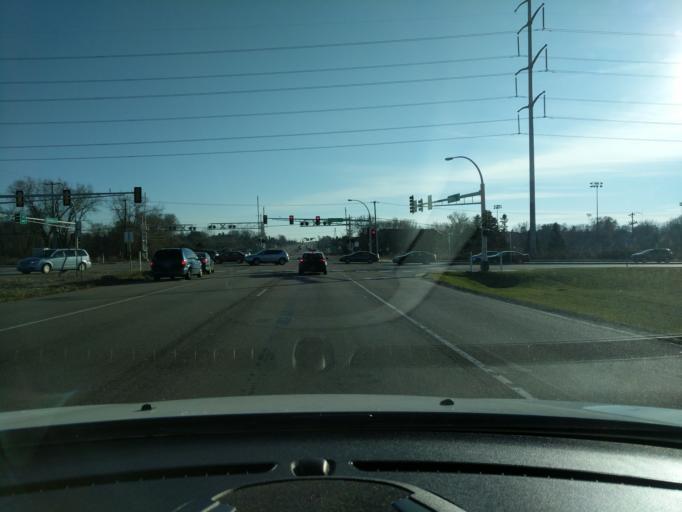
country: US
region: Minnesota
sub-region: Ramsey County
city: Roseville
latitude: 45.0216
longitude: -93.1672
